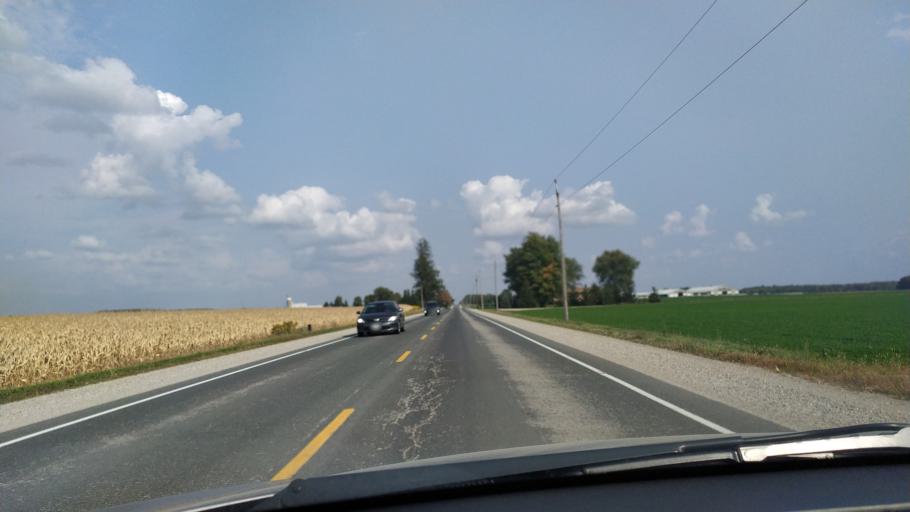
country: CA
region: Ontario
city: Stratford
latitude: 43.3514
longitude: -80.8566
